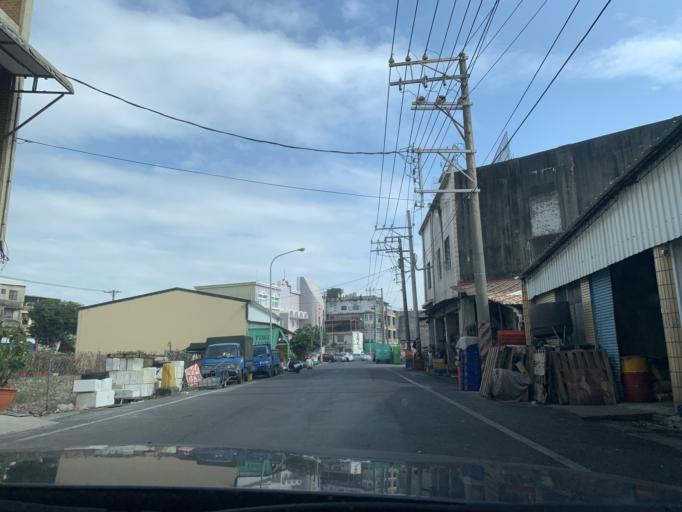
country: TW
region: Taiwan
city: Fengshan
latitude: 22.4669
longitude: 120.4451
